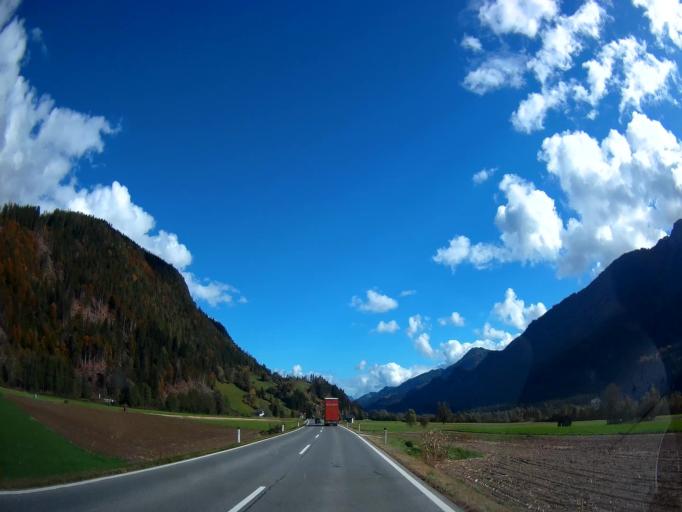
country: AT
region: Carinthia
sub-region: Politischer Bezirk Spittal an der Drau
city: Irschen
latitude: 46.7406
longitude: 13.0475
